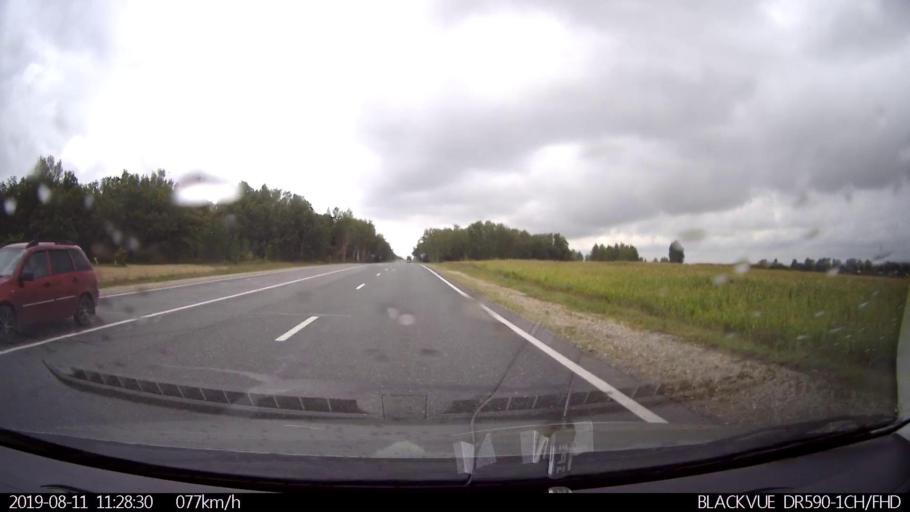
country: RU
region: Ulyanovsk
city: Krasnyy Gulyay
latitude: 54.0819
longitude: 48.2305
